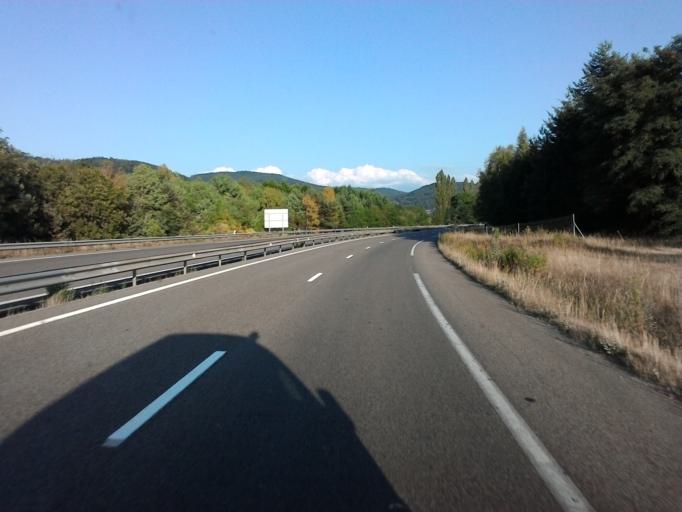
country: FR
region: Lorraine
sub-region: Departement des Vosges
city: Pouxeux
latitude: 48.1062
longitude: 6.5859
